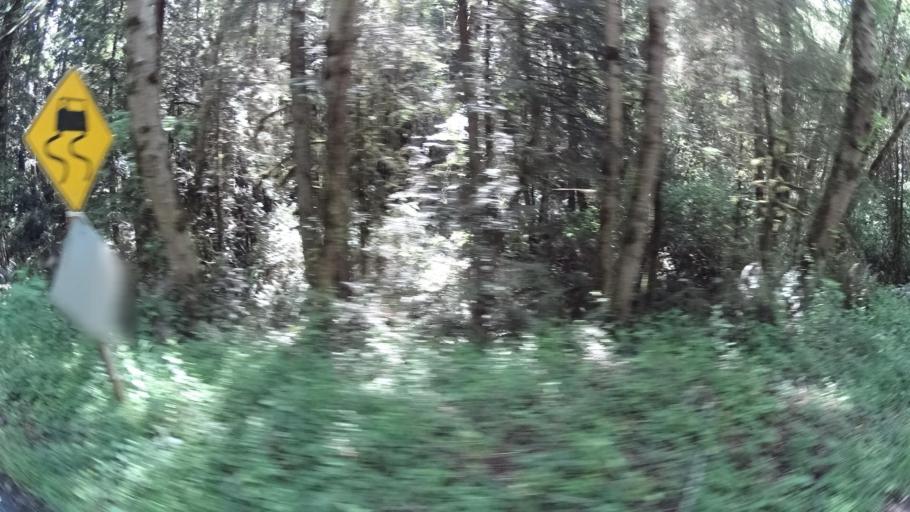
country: US
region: California
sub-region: Humboldt County
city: McKinleyville
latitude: 40.9690
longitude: -124.0660
